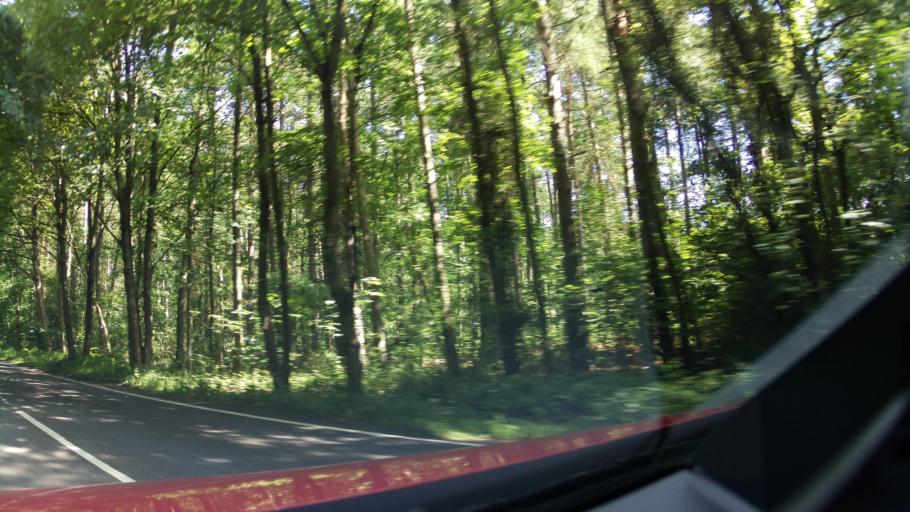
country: GB
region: England
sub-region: North Lincolnshire
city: Manton
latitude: 53.5410
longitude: -0.5768
